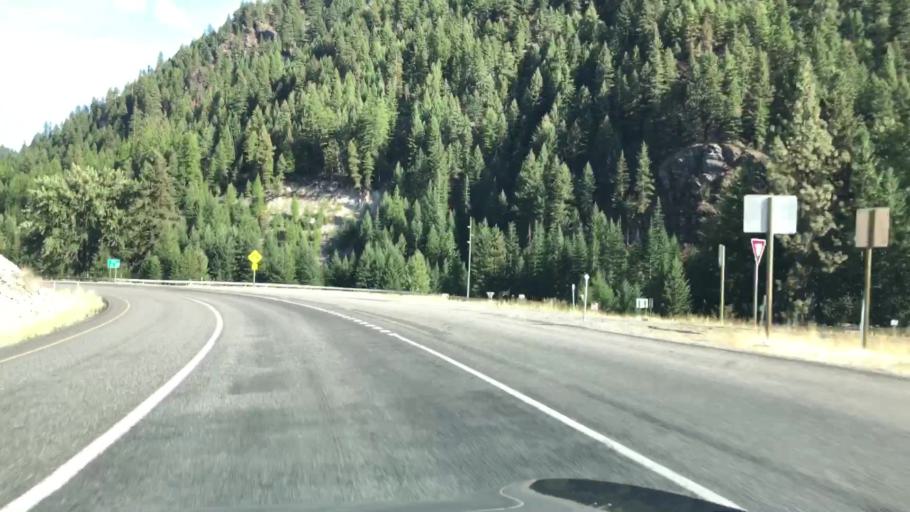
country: US
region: Montana
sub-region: Sanders County
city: Thompson Falls
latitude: 47.3129
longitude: -115.2342
